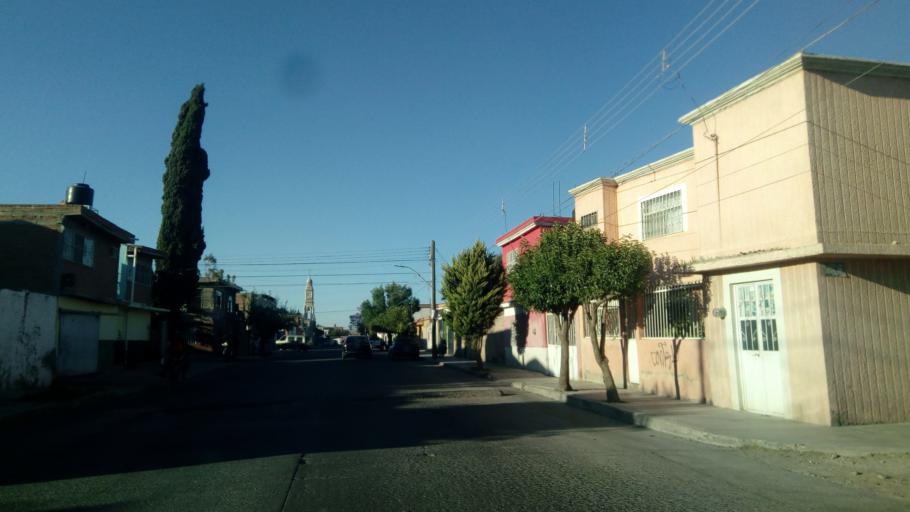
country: MX
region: Durango
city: Victoria de Durango
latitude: 23.9991
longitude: -104.6751
